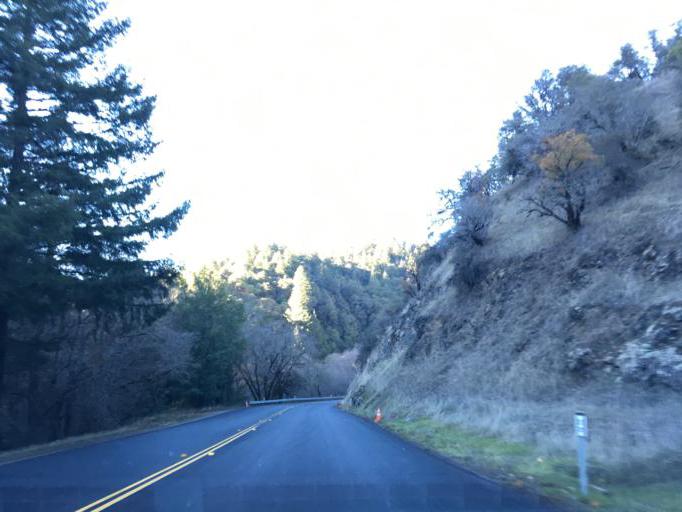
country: US
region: California
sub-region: Mendocino County
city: Laytonville
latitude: 39.8162
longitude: -123.5619
